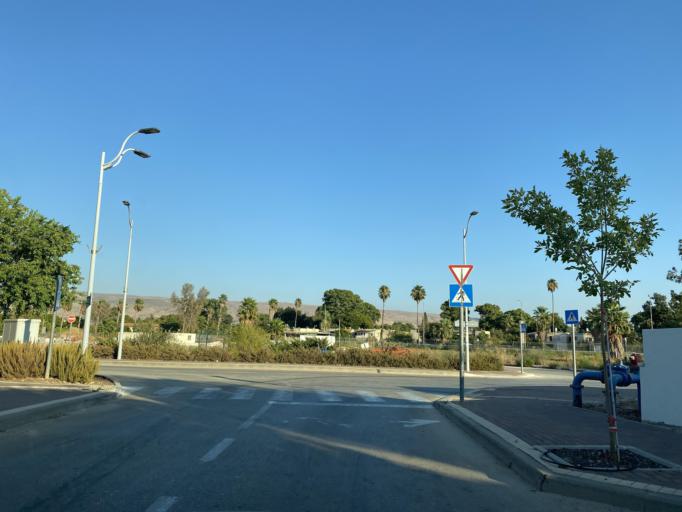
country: IL
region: Northern District
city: Qiryat Shemona
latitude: 33.1752
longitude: 35.6064
